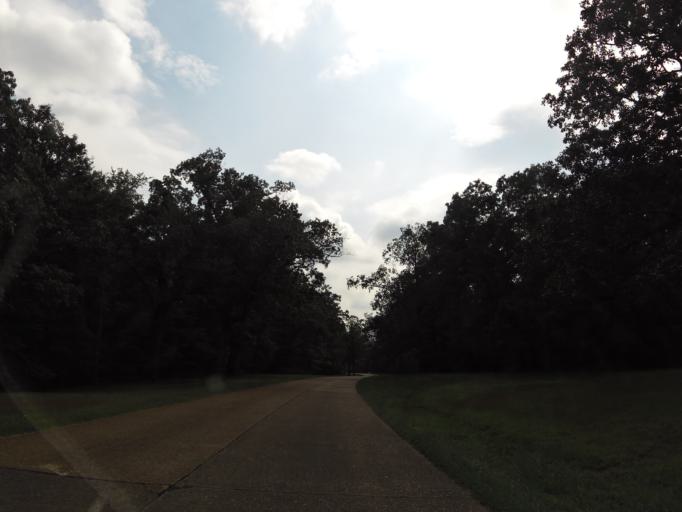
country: US
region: Tennessee
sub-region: Hardin County
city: Crump
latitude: 35.1463
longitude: -88.3313
